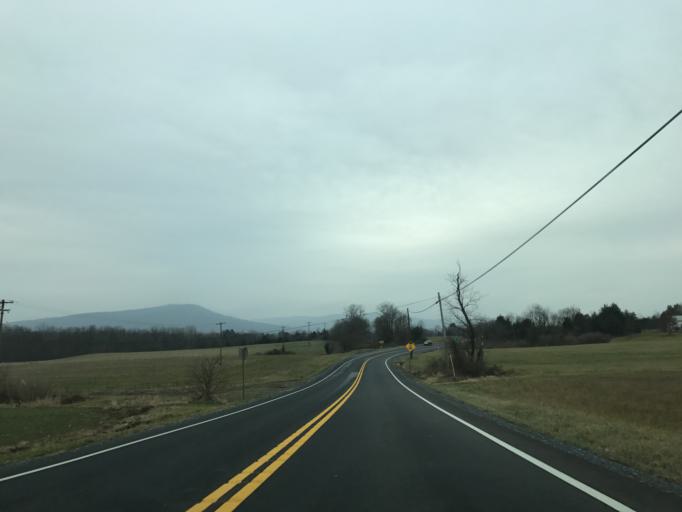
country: US
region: Maryland
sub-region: Frederick County
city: Emmitsburg
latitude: 39.7011
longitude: -77.3076
